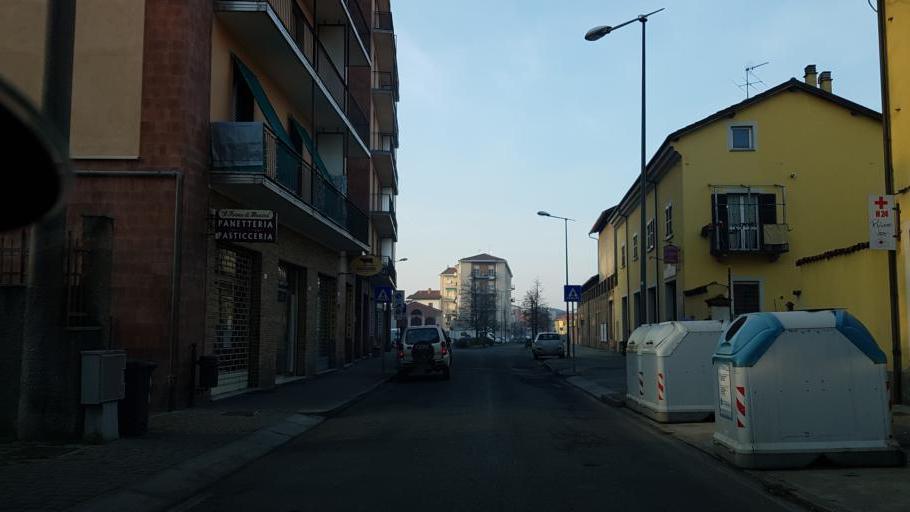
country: IT
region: Piedmont
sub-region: Provincia di Alessandria
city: Novi Ligure
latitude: 44.7620
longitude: 8.7801
